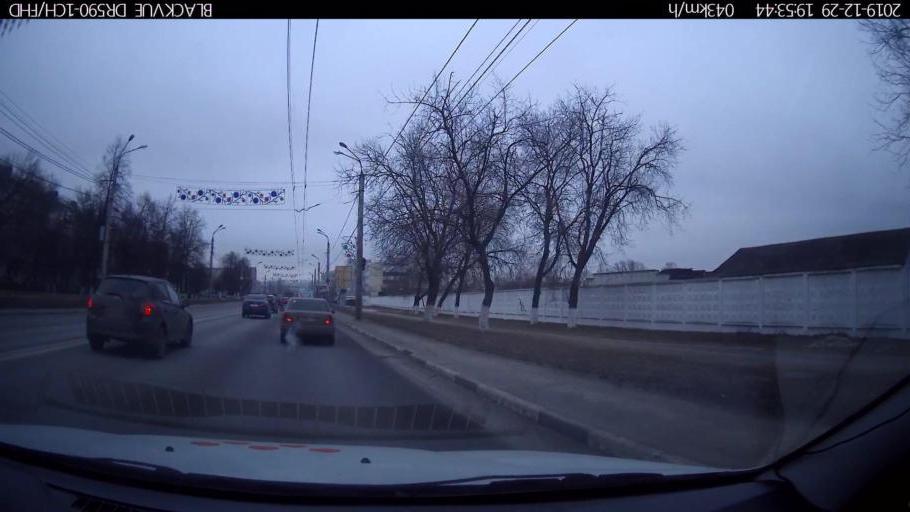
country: RU
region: Nizjnij Novgorod
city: Nizhniy Novgorod
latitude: 56.3227
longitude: 43.9201
